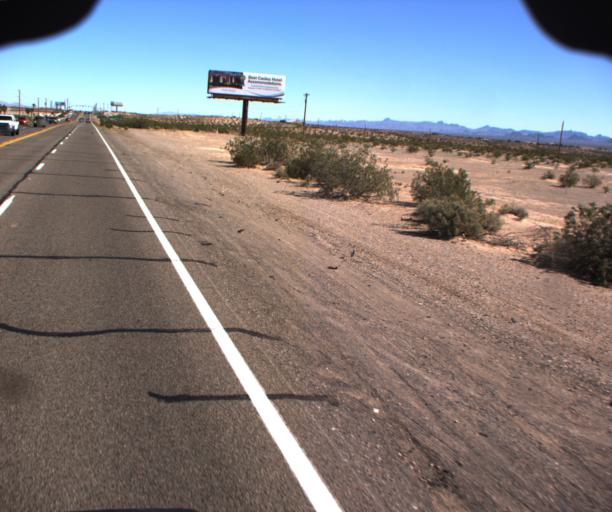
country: US
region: Arizona
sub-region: Mohave County
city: Mohave Valley
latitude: 34.9749
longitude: -114.5979
